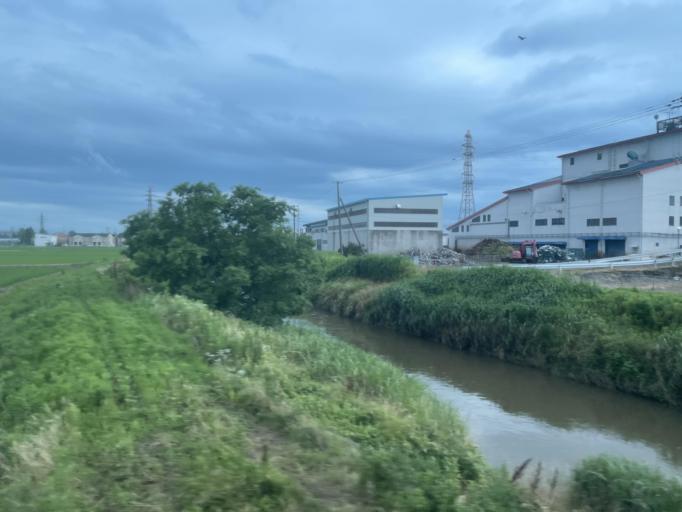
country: JP
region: Niigata
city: Yoshida-kasugacho
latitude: 37.6831
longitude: 138.9030
